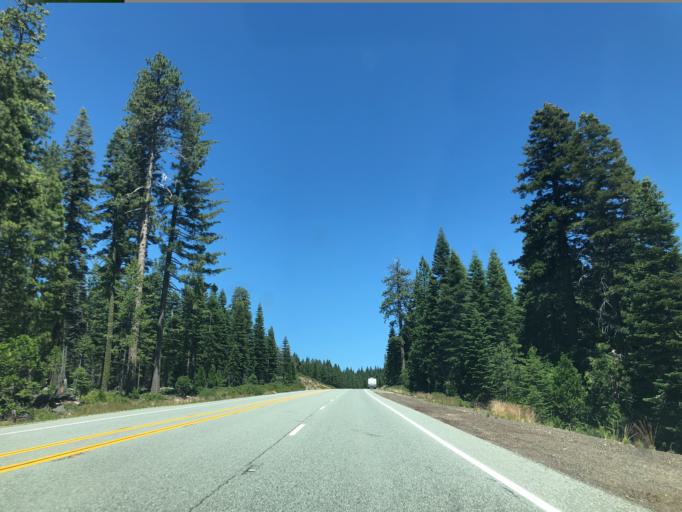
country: US
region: California
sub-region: Shasta County
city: Shingletown
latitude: 40.5389
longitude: -121.6103
